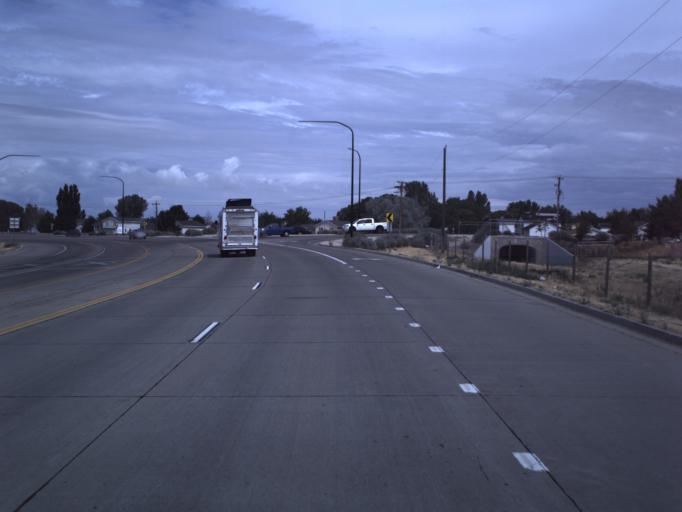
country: US
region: Utah
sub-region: Davis County
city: Clearfield
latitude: 41.1095
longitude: -112.0319
